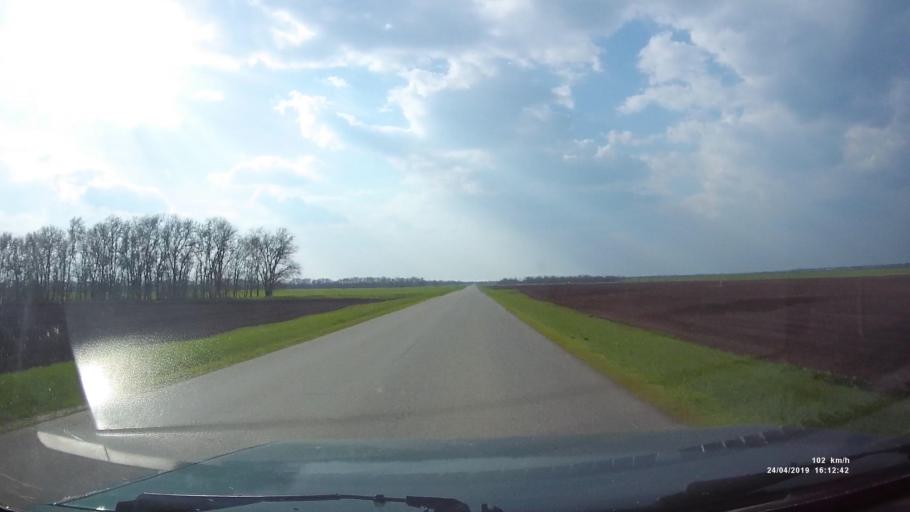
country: RU
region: Rostov
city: Sovetskoye
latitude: 46.7350
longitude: 42.2321
